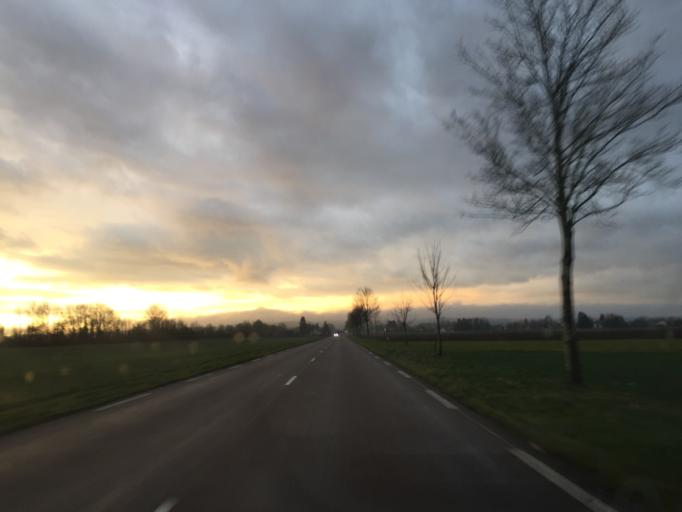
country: FR
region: Franche-Comte
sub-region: Departement du Jura
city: Choisey
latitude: 47.0327
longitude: 5.4952
